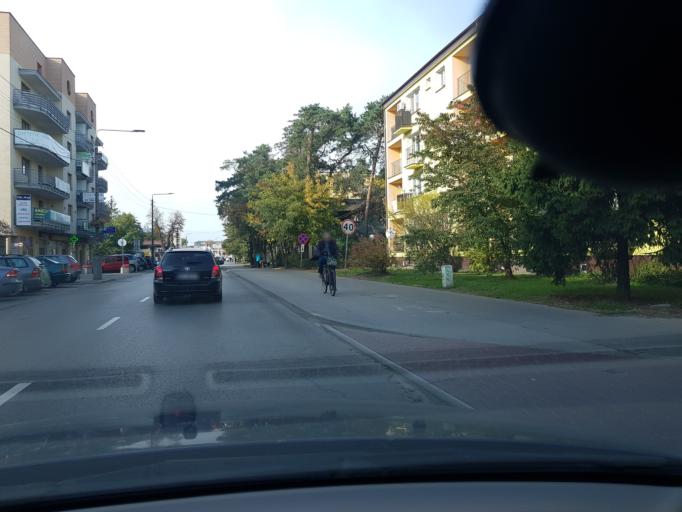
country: PL
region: Masovian Voivodeship
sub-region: Powiat otwocki
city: Otwock
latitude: 52.1043
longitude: 21.2646
